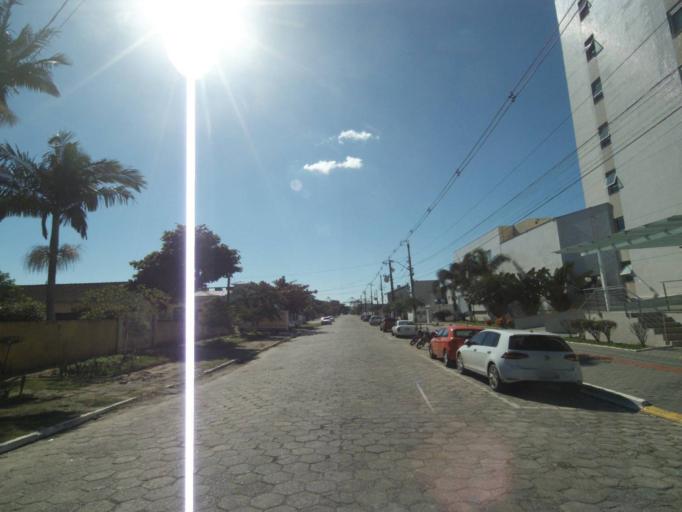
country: BR
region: Parana
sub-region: Paranagua
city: Paranagua
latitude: -25.5141
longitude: -48.5041
